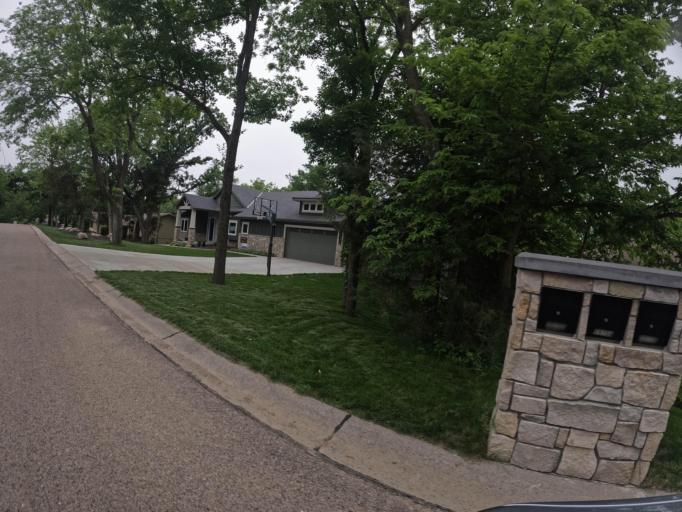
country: US
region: Nebraska
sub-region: Sarpy County
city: Offutt Air Force Base
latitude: 41.0515
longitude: -95.9696
